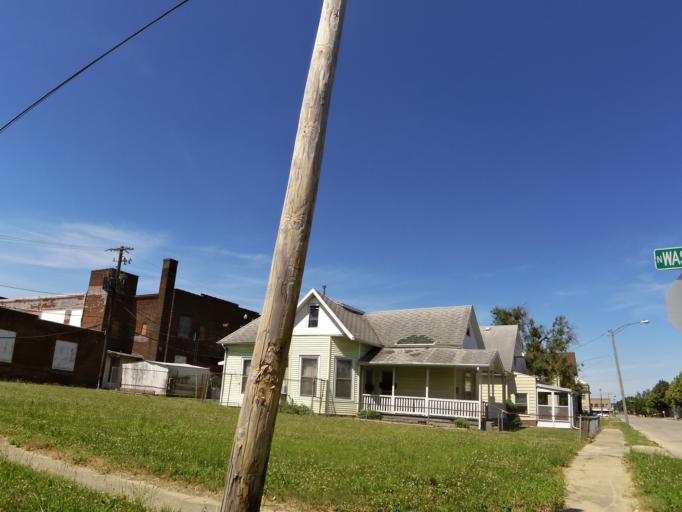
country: US
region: Illinois
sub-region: Vermilion County
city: Danville
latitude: 40.1291
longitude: -87.6261
